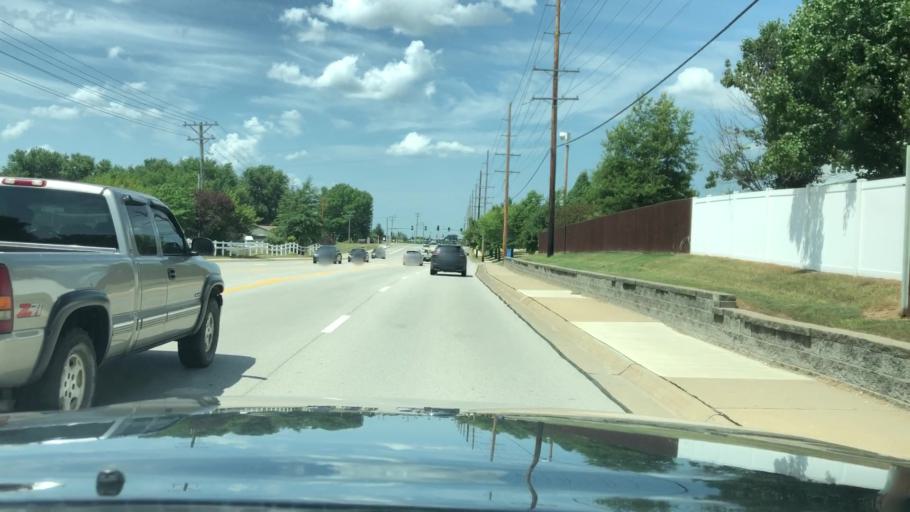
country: US
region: Missouri
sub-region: Saint Charles County
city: O'Fallon
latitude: 38.7875
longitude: -90.6668
